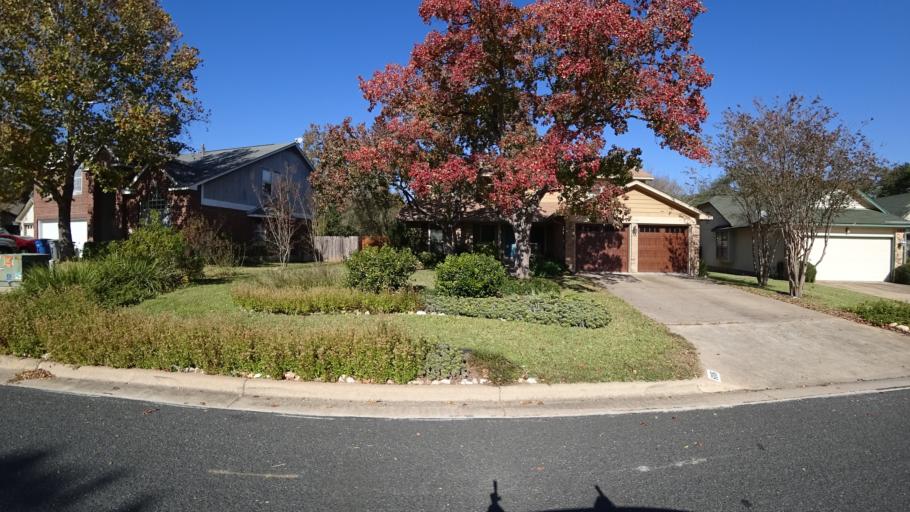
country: US
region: Texas
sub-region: Travis County
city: Shady Hollow
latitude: 30.2215
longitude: -97.8675
